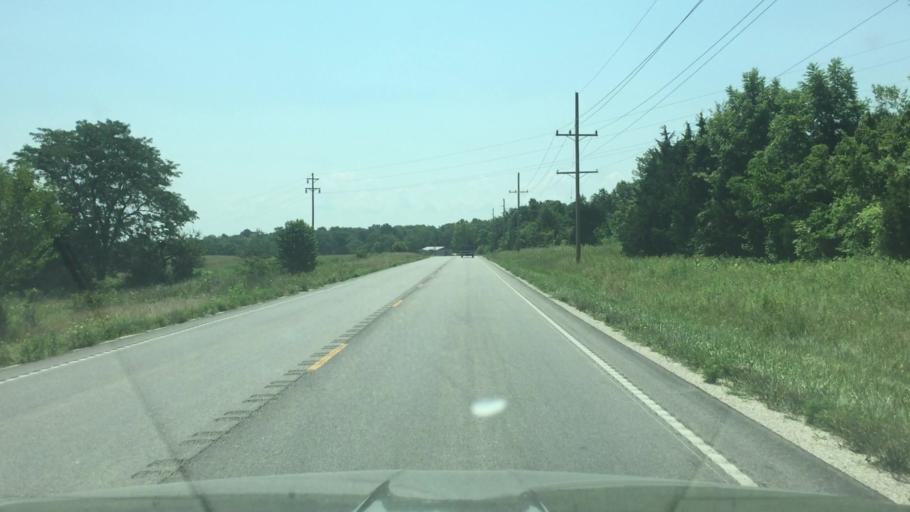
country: US
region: Missouri
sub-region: Miller County
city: Eldon
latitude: 38.3831
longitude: -92.6844
